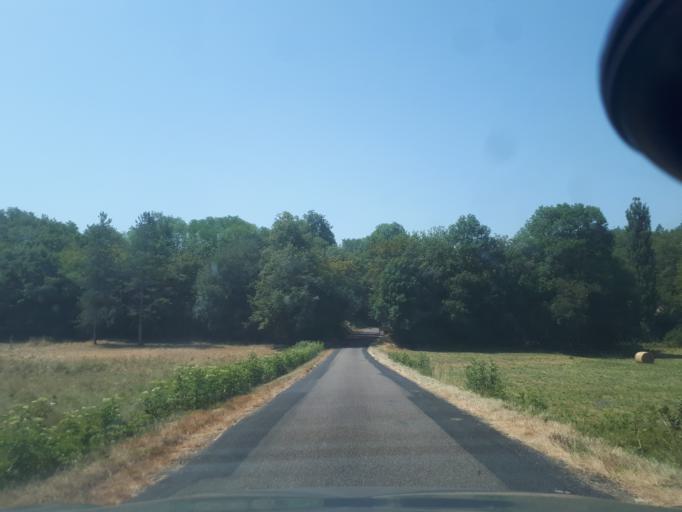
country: FR
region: Midi-Pyrenees
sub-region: Departement du Lot
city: Souillac
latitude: 44.8479
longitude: 1.4055
